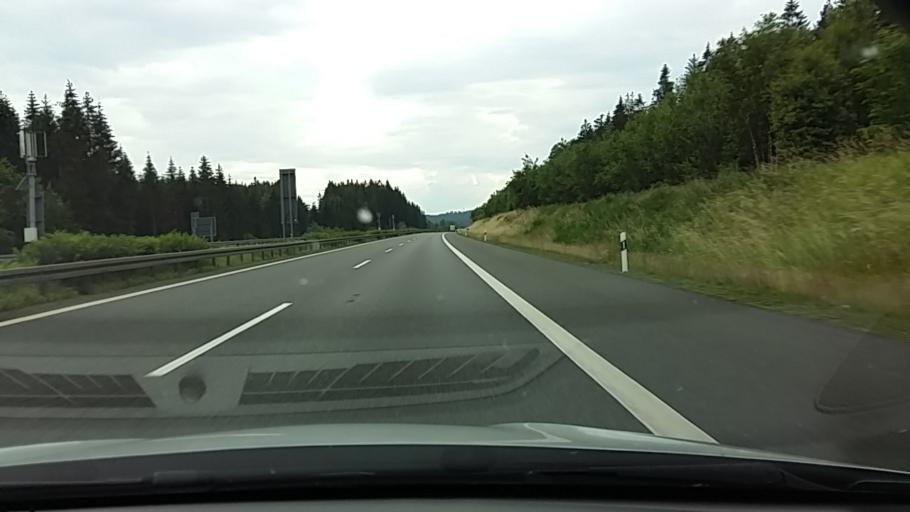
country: DE
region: Bavaria
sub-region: Upper Palatinate
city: Pleystein
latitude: 49.6279
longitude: 12.4427
